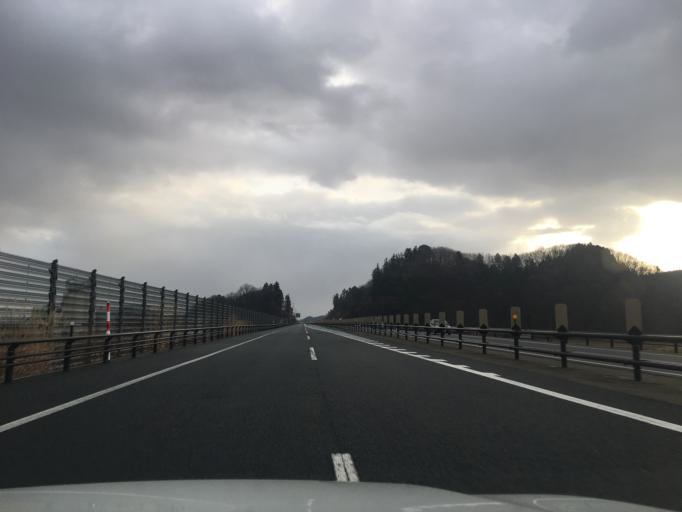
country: JP
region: Yamagata
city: Tsuruoka
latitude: 38.7063
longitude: 139.7294
